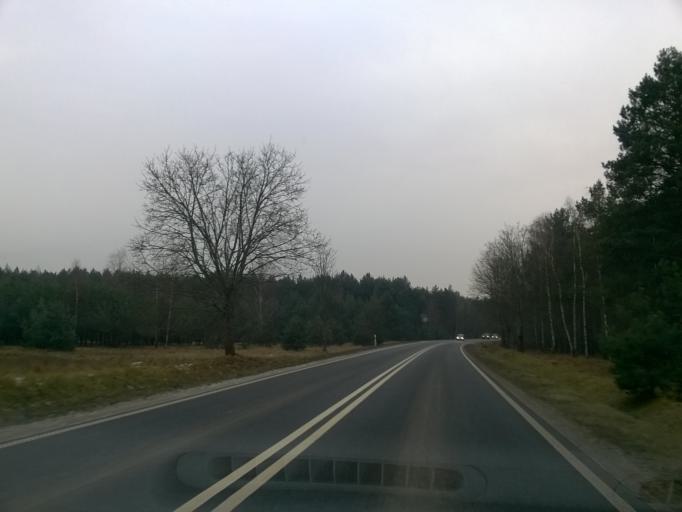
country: PL
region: Kujawsko-Pomorskie
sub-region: Powiat nakielski
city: Naklo nad Notecia
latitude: 53.0762
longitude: 17.5846
